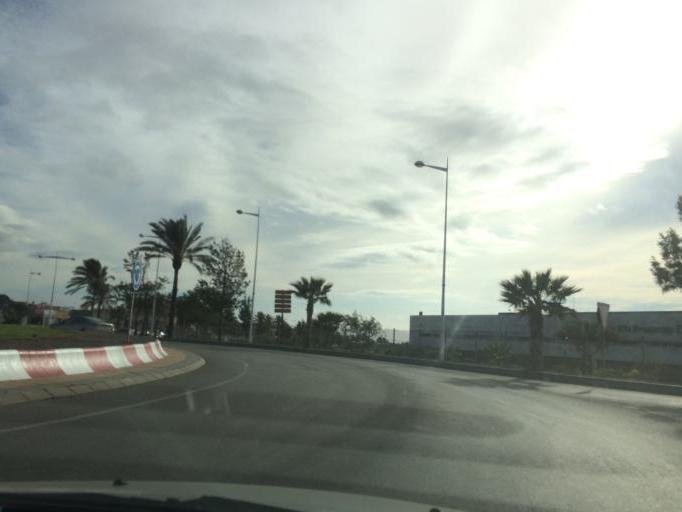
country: ES
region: Andalusia
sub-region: Provincia de Almeria
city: Retamar
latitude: 36.8519
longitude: -2.3133
